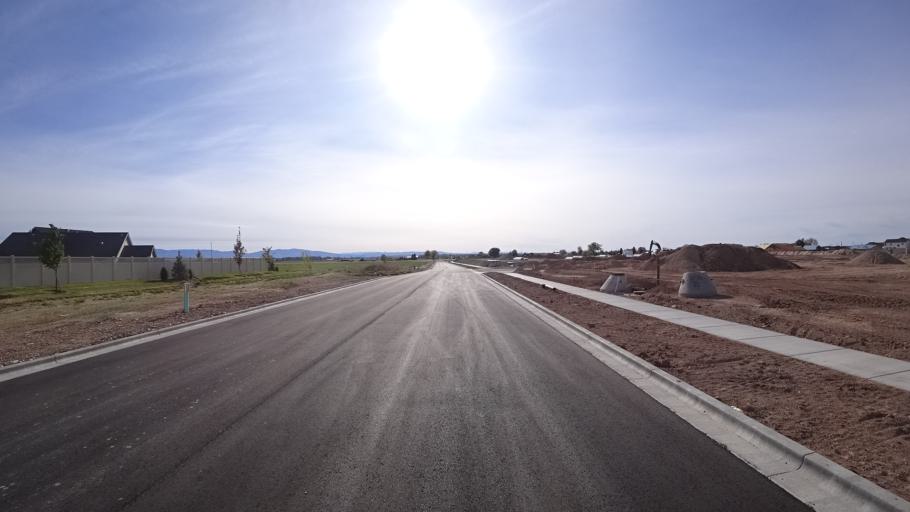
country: US
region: Idaho
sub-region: Ada County
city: Kuna
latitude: 43.5101
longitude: -116.3999
